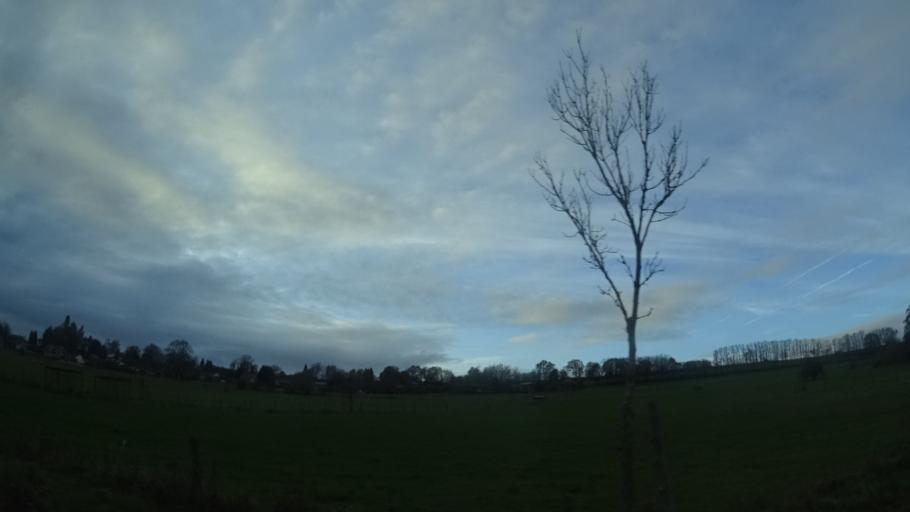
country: DE
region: Hesse
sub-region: Regierungsbezirk Giessen
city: Grebenhain
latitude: 50.4779
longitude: 9.3877
